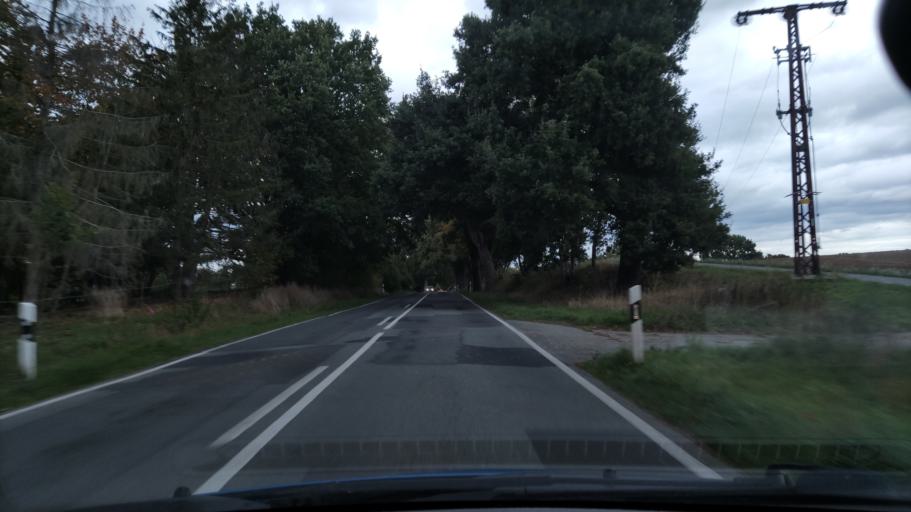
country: DE
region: Mecklenburg-Vorpommern
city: Lubtheen
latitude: 53.3896
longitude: 10.9659
